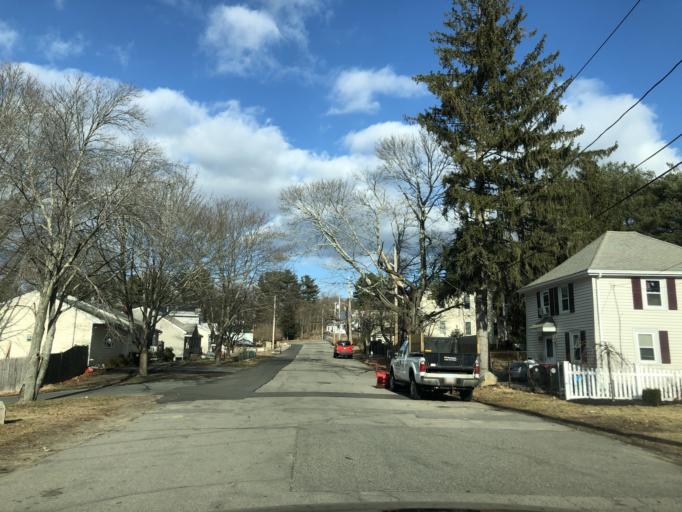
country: US
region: Massachusetts
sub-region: Plymouth County
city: Brockton
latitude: 42.1015
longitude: -71.0100
